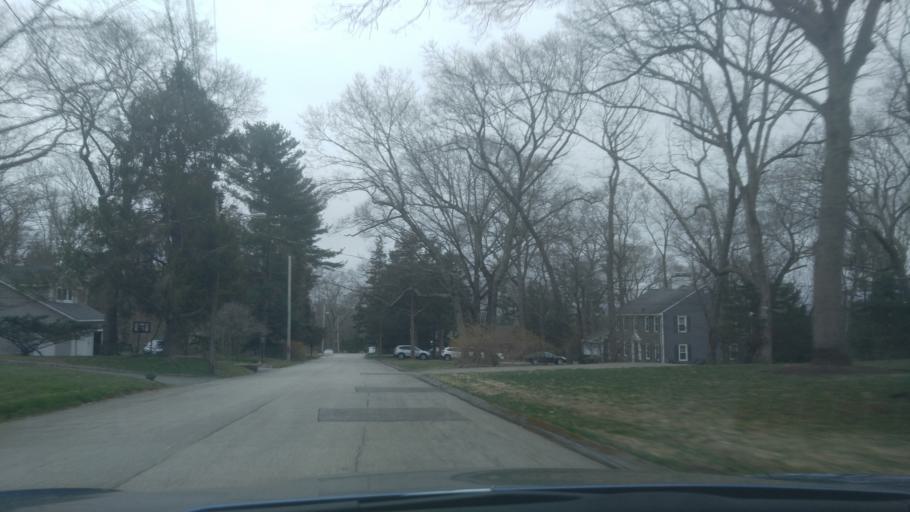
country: US
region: Rhode Island
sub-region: Kent County
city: East Greenwich
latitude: 41.6694
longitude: -71.4621
